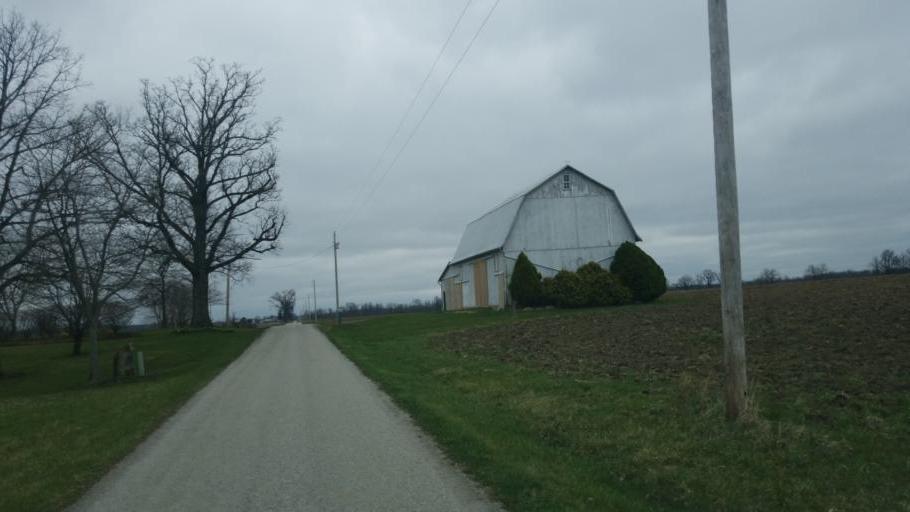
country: US
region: Ohio
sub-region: Hardin County
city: Forest
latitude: 40.6527
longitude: -83.3905
